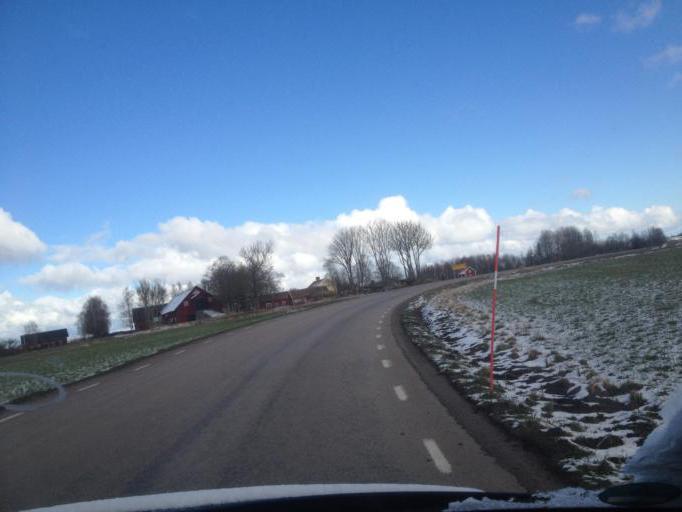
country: SE
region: OEstergoetland
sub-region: Mjolby Kommun
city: Mantorp
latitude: 58.4116
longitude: 15.3039
